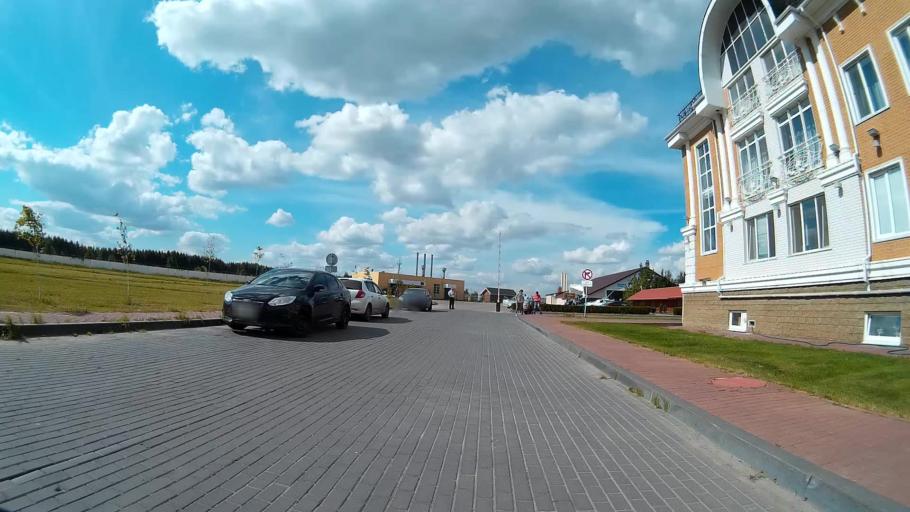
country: RU
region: Ulyanovsk
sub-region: Ulyanovskiy Rayon
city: Ulyanovsk
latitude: 54.2728
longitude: 48.2652
